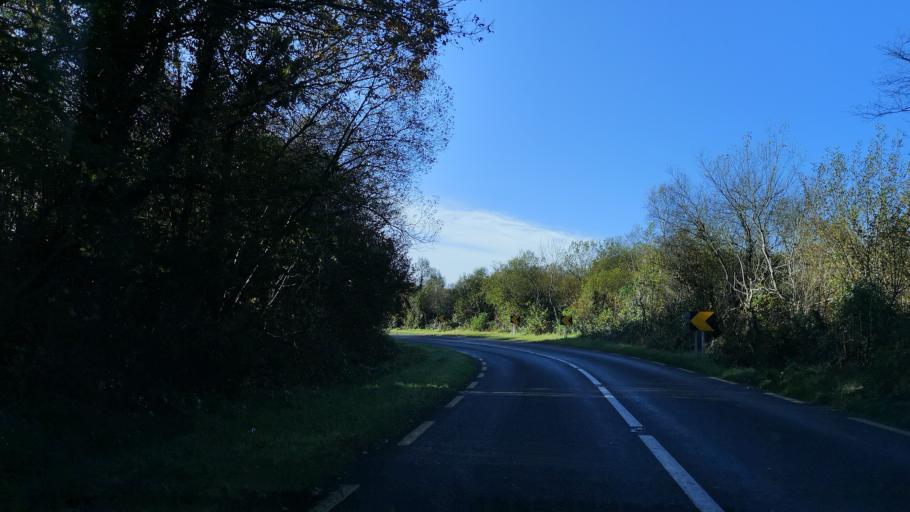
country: IE
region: Connaught
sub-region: Maigh Eo
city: Westport
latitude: 53.7551
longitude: -9.5564
